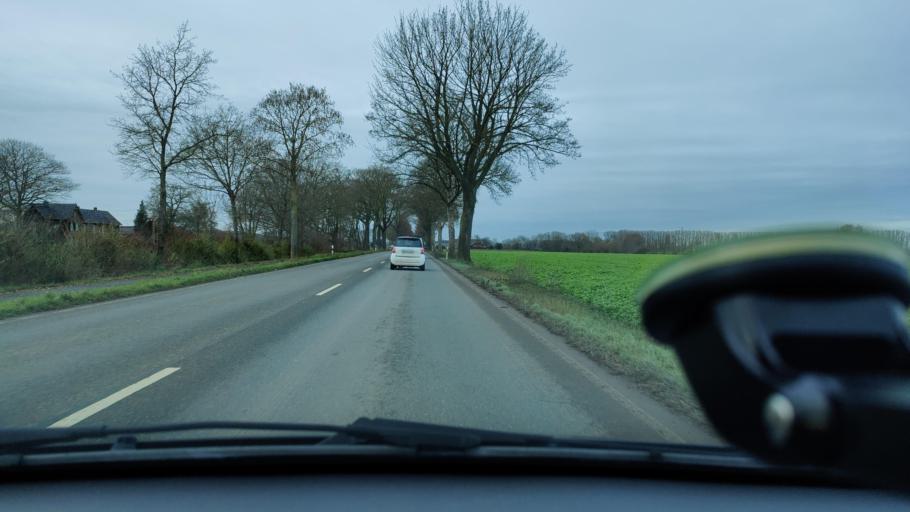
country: DE
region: North Rhine-Westphalia
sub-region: Regierungsbezirk Dusseldorf
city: Xanten
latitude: 51.6756
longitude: 6.4250
